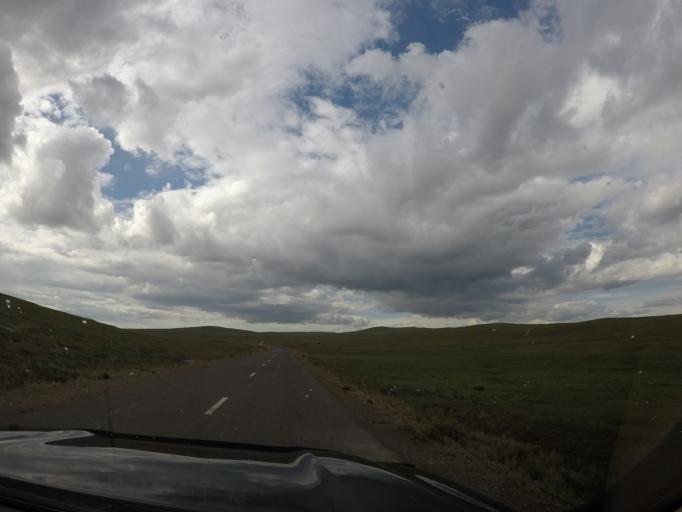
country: MN
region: Hentiy
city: Modot
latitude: 47.5423
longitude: 109.3889
